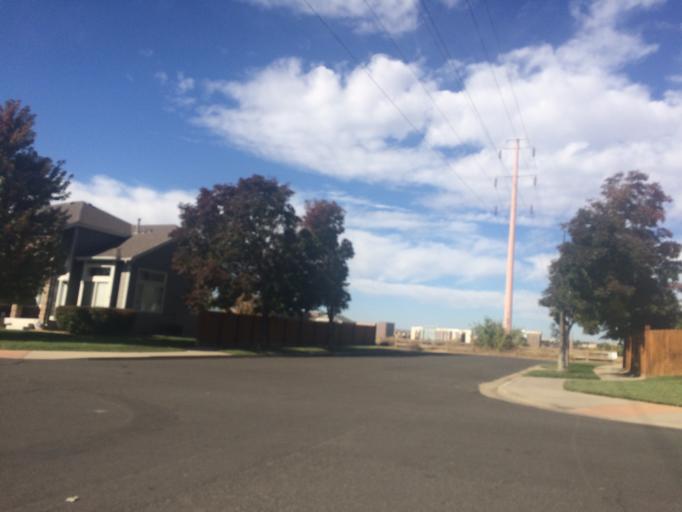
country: US
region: Colorado
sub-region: Broomfield County
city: Broomfield
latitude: 39.8777
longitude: -105.0717
